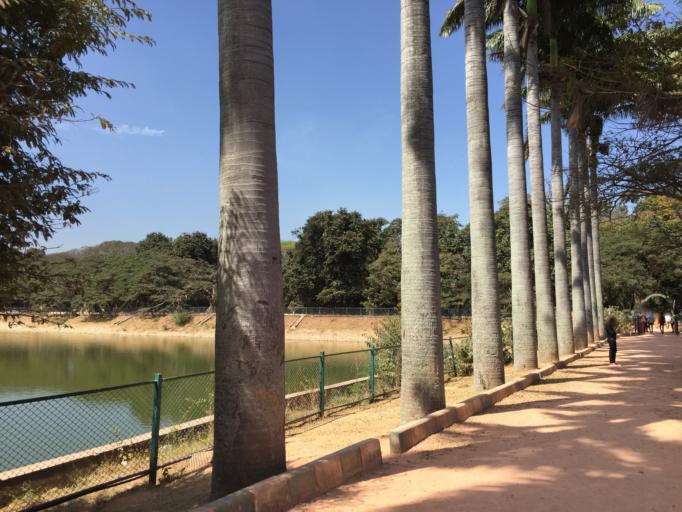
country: IN
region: Karnataka
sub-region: Bangalore Urban
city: Bangalore
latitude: 12.9467
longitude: 77.5853
